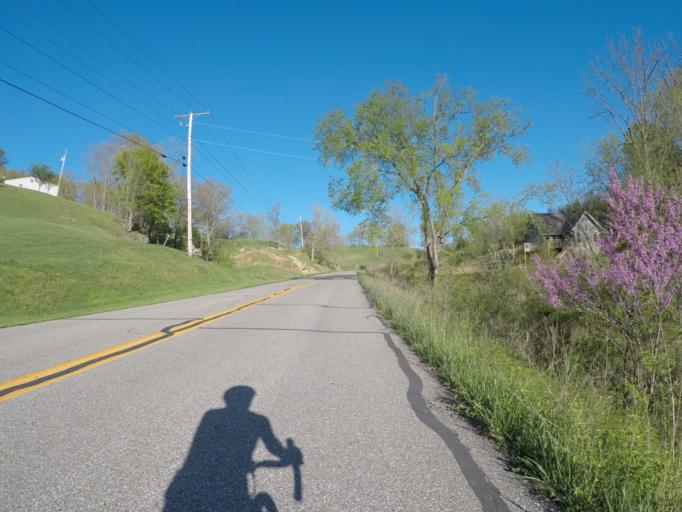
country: US
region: Kentucky
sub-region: Boyd County
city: Catlettsburg
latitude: 38.3706
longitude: -82.6568
